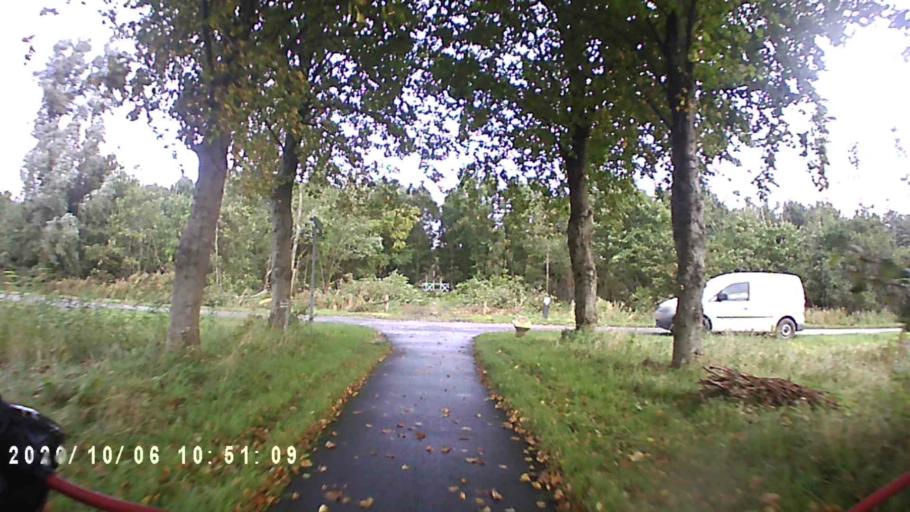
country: NL
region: Groningen
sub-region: Gemeente Zuidhorn
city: Oldehove
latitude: 53.3664
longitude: 6.4111
